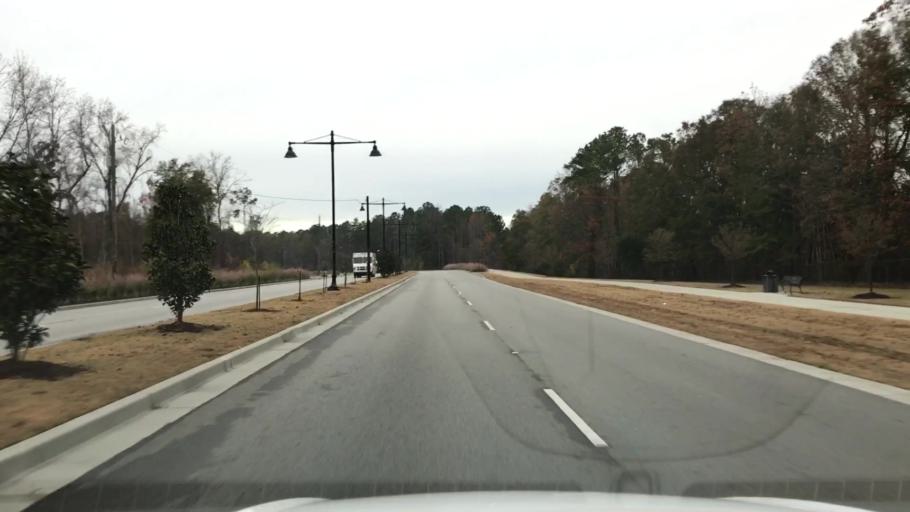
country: US
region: South Carolina
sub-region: Berkeley County
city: Goose Creek
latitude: 32.9570
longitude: -80.0686
